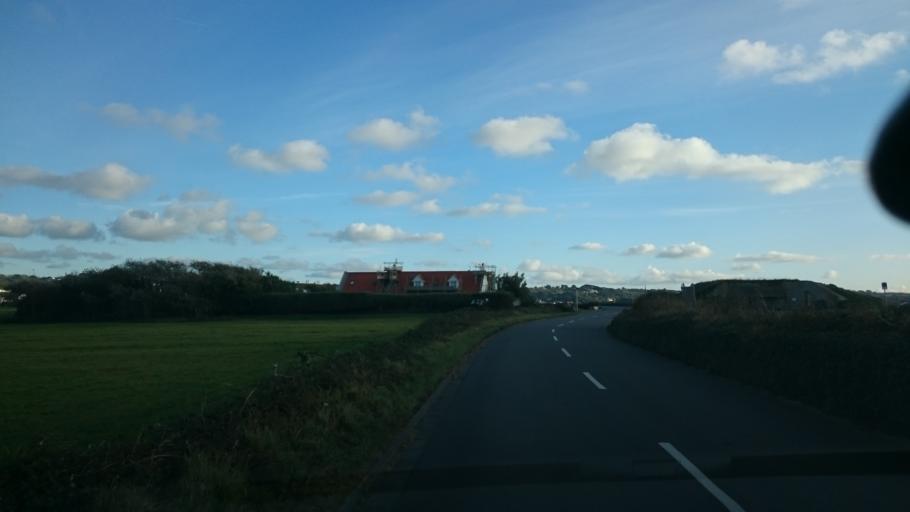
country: GG
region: St Peter Port
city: Saint Peter Port
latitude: 49.4557
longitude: -2.6533
